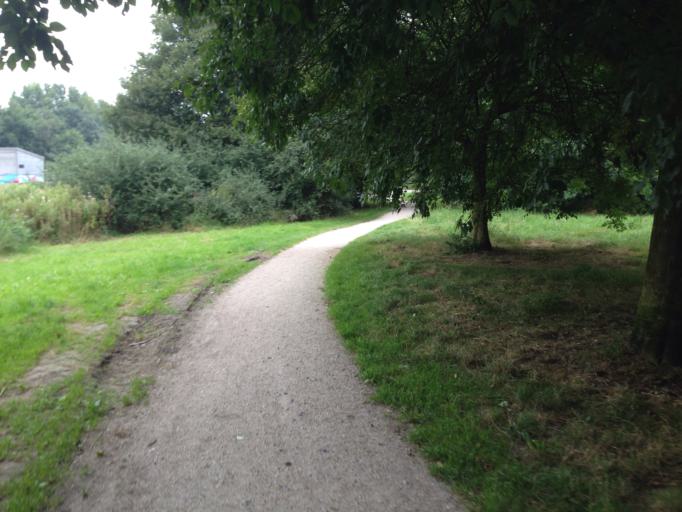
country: NL
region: Flevoland
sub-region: Gemeente Almere
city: Almere Stad
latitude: 52.3848
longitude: 5.2378
